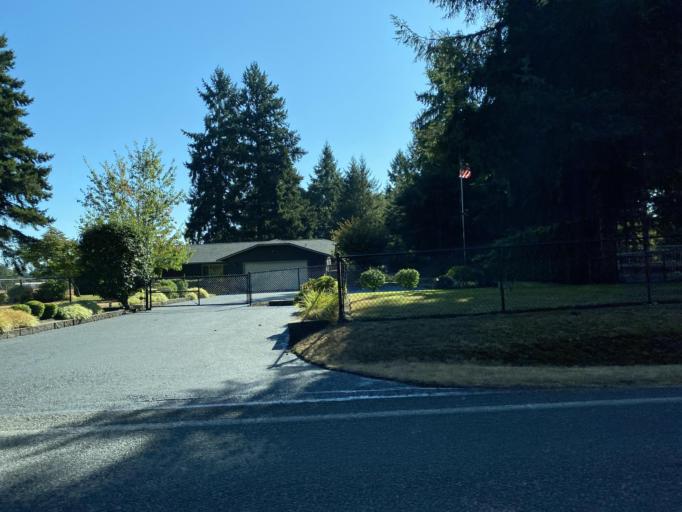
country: US
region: Washington
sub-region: Thurston County
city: Tanglewilde-Thompson Place
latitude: 47.0086
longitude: -122.7386
